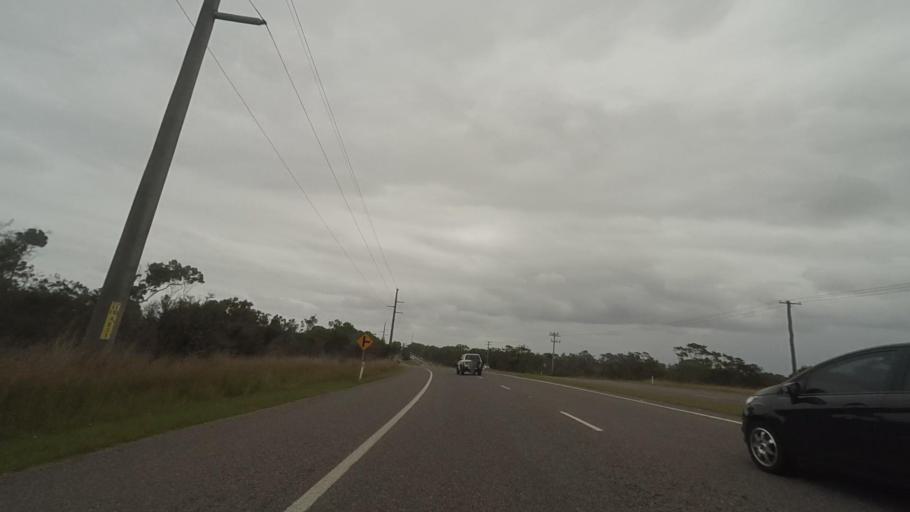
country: AU
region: New South Wales
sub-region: Wyong Shire
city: Kingfisher Shores
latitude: -33.1858
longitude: 151.5860
